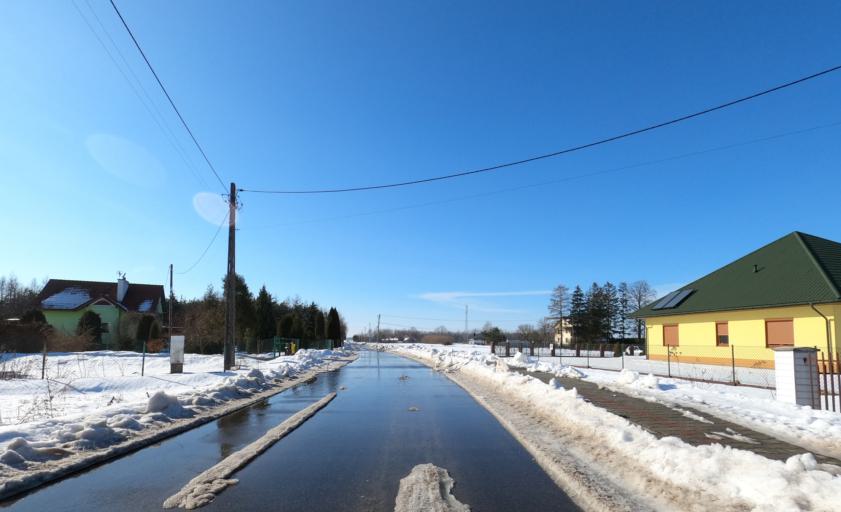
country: PL
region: Subcarpathian Voivodeship
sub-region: Powiat debicki
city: Brzeznica
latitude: 50.0851
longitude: 21.5186
